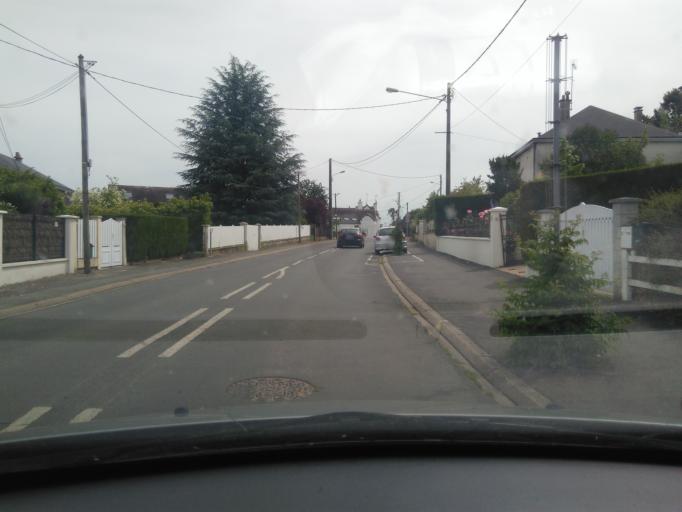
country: FR
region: Centre
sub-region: Departement d'Indre-et-Loire
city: Amboise
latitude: 47.4036
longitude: 0.9929
